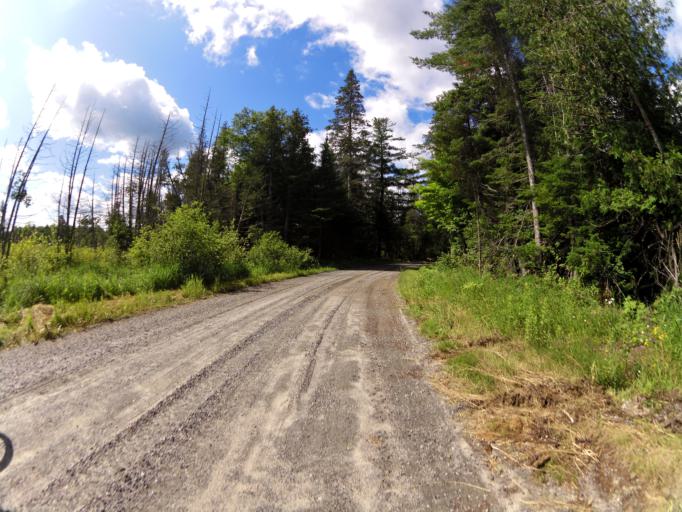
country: CA
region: Ontario
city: Perth
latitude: 45.0731
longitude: -76.4702
